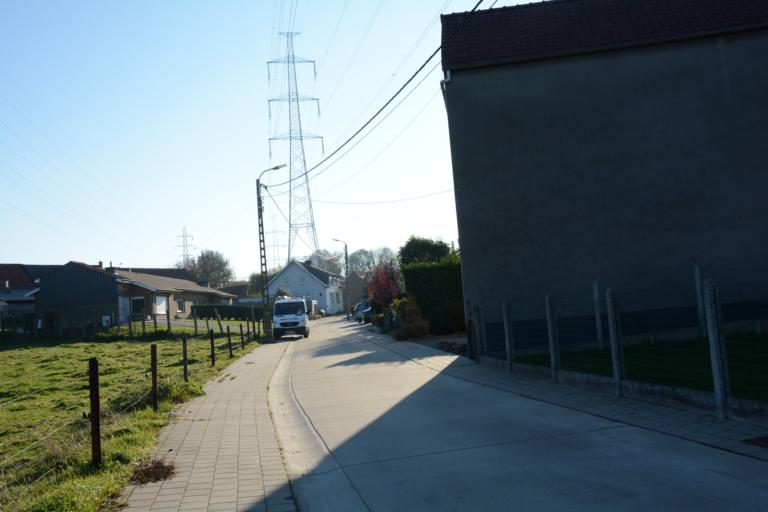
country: BE
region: Flanders
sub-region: Provincie Vlaams-Brabant
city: Asse
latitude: 50.9010
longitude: 4.2337
